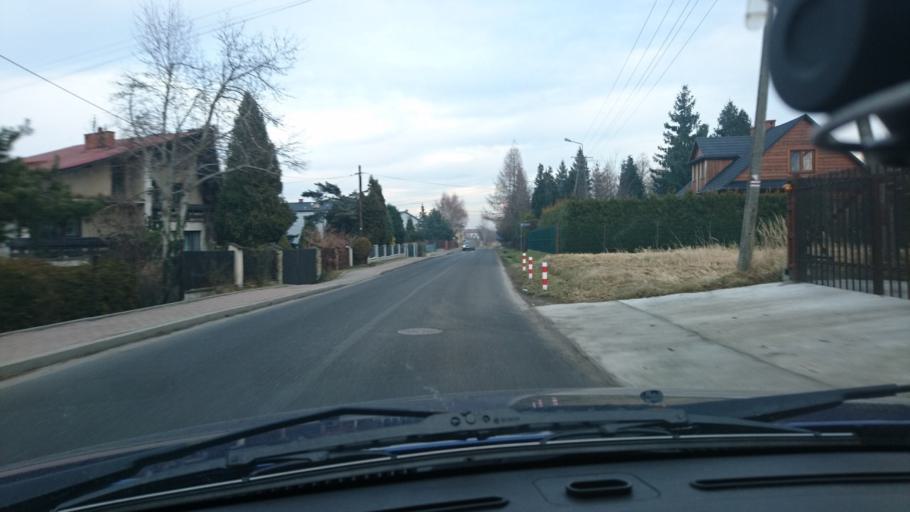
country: PL
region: Silesian Voivodeship
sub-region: Powiat bielski
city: Buczkowice
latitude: 49.7266
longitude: 19.0646
